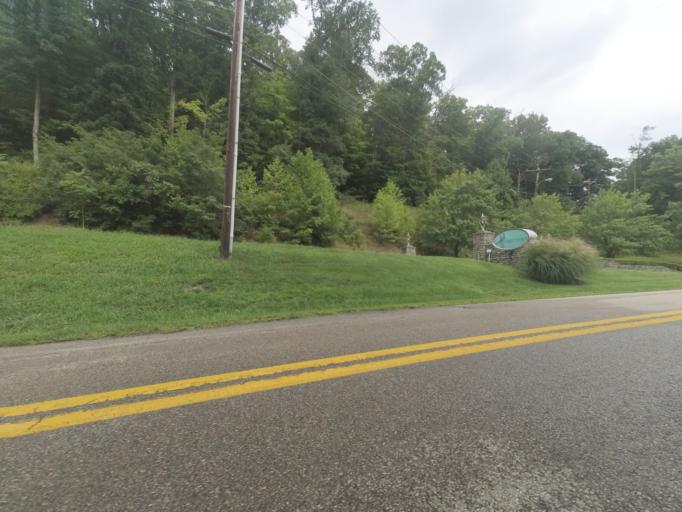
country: US
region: West Virginia
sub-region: Cabell County
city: Huntington
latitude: 38.3957
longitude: -82.4565
